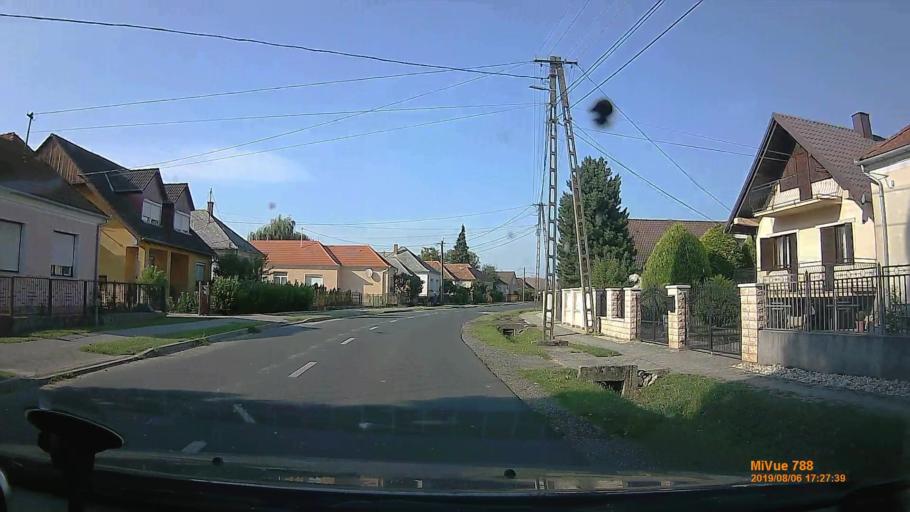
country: HR
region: Medimurska
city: Kotoriba
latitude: 46.3867
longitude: 16.8340
